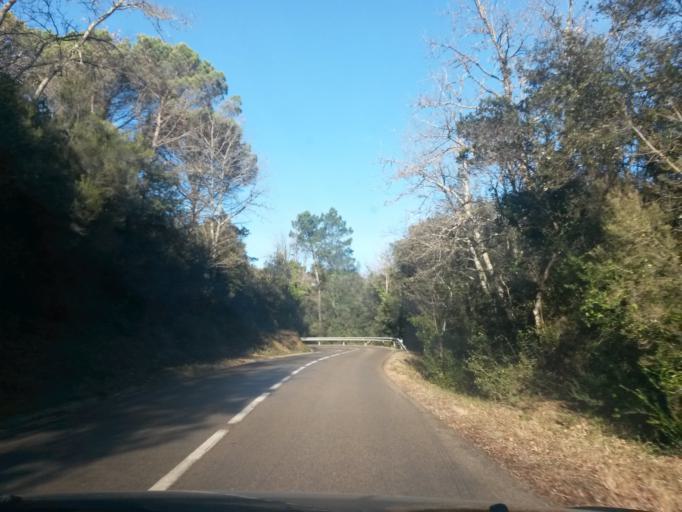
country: ES
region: Catalonia
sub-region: Provincia de Girona
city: Angles
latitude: 41.9958
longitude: 2.6714
